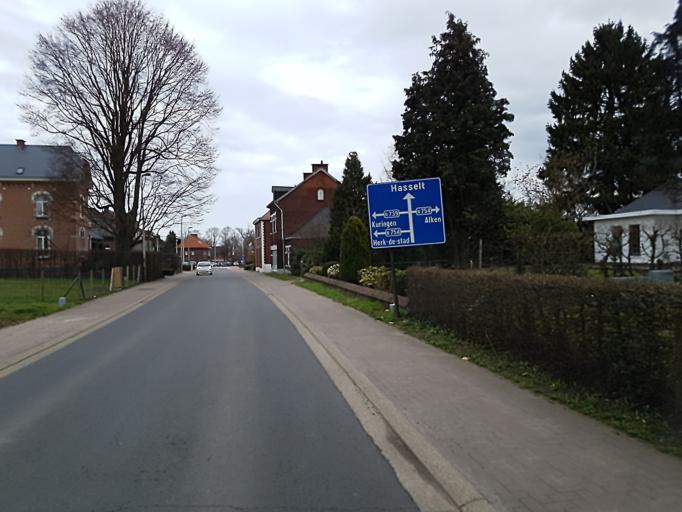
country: BE
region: Flanders
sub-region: Provincie Limburg
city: Alken
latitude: 50.9141
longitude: 5.2471
